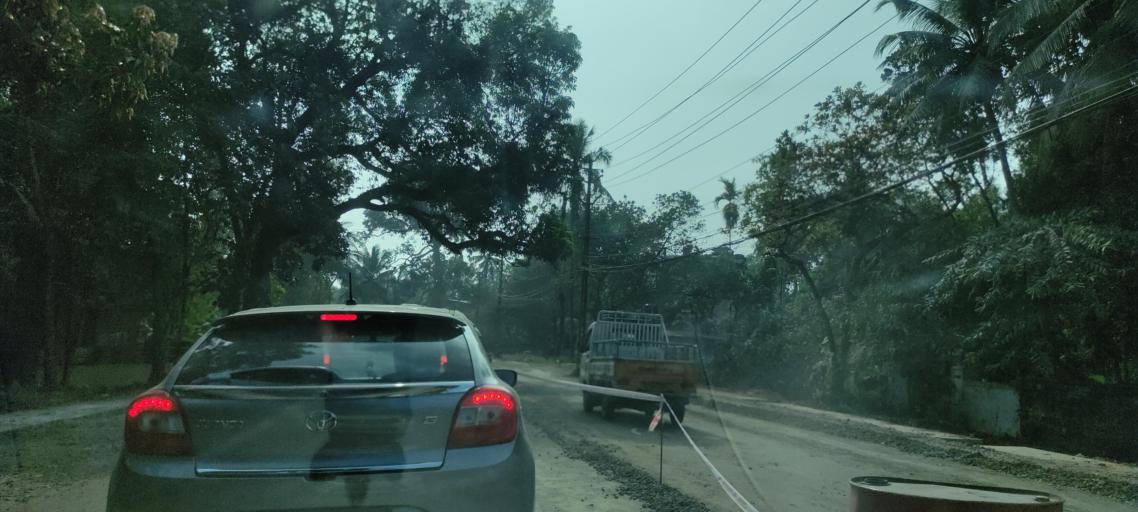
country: IN
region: Kerala
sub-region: Pattanamtitta
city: Tiruvalla
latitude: 9.3686
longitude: 76.5476
